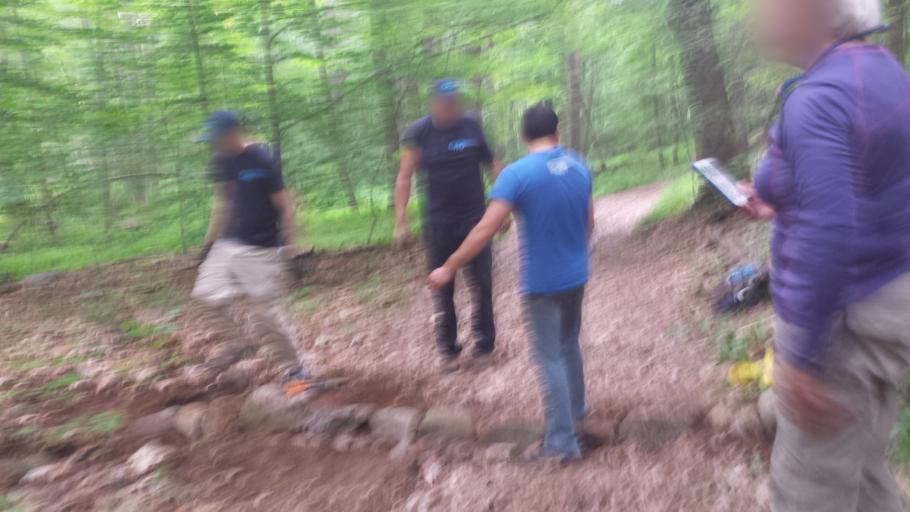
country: US
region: New York
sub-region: Westchester County
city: Pound Ridge
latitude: 41.2624
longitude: -73.5783
